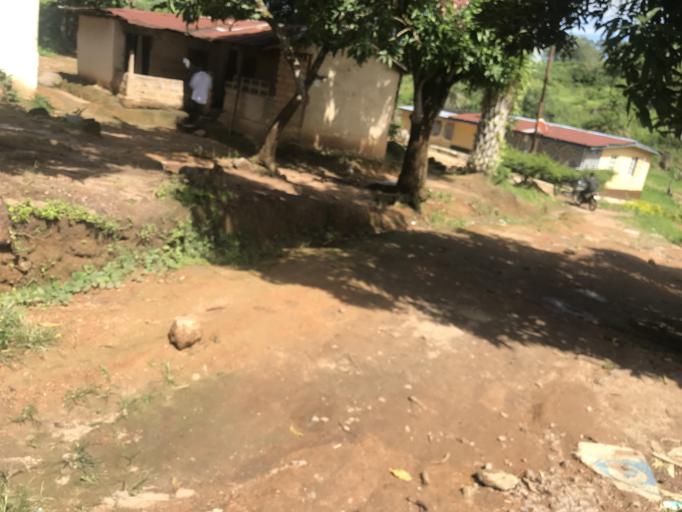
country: SL
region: Eastern Province
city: Koidu
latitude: 8.6477
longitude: -10.9882
